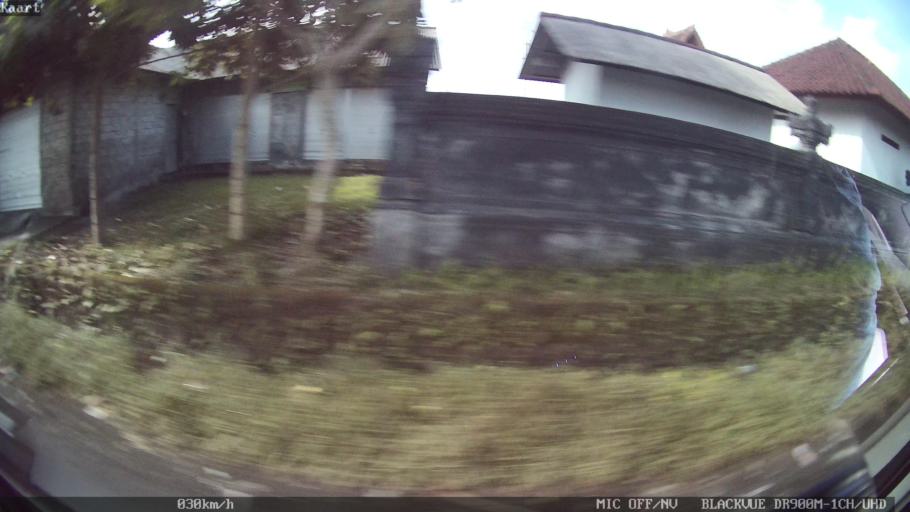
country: ID
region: Bali
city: Banjar Pekenjelodan
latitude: -8.5707
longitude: 115.1862
